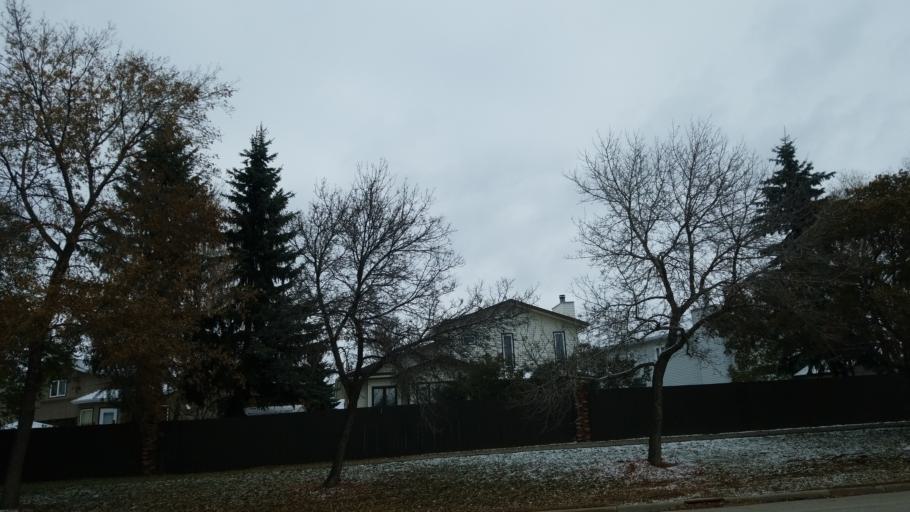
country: CA
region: Alberta
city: Sherwood Park
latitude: 53.5249
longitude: -113.2748
